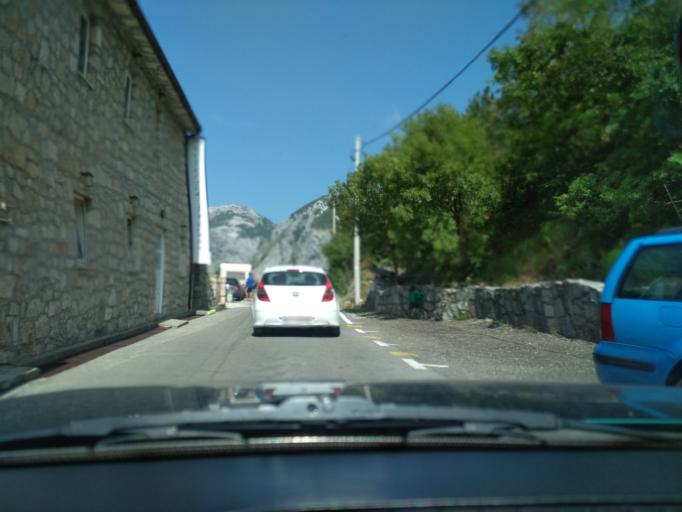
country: ME
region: Kotor
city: Kotor
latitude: 42.4199
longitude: 18.7946
